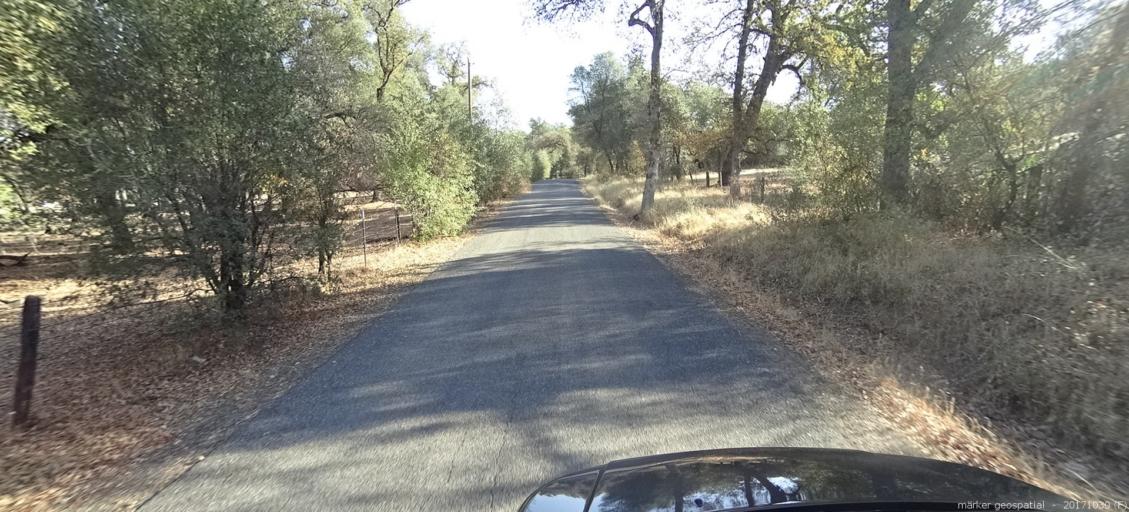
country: US
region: California
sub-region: Shasta County
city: Palo Cedro
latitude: 40.5655
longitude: -122.1464
